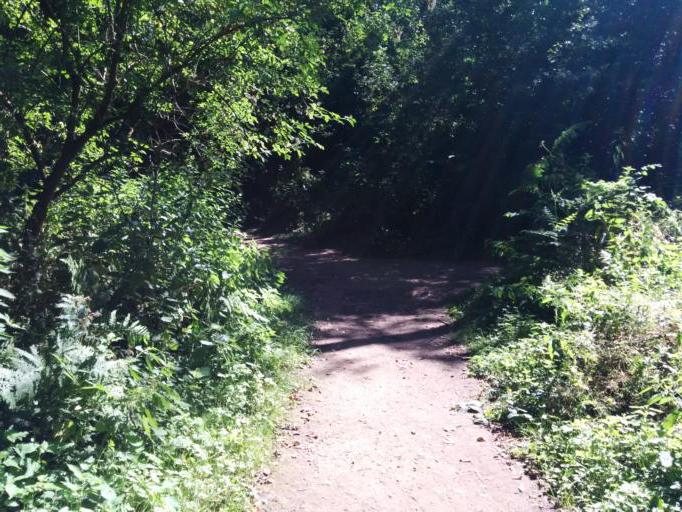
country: GB
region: England
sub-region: Surrey
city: Bramley
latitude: 51.1627
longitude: -0.5768
